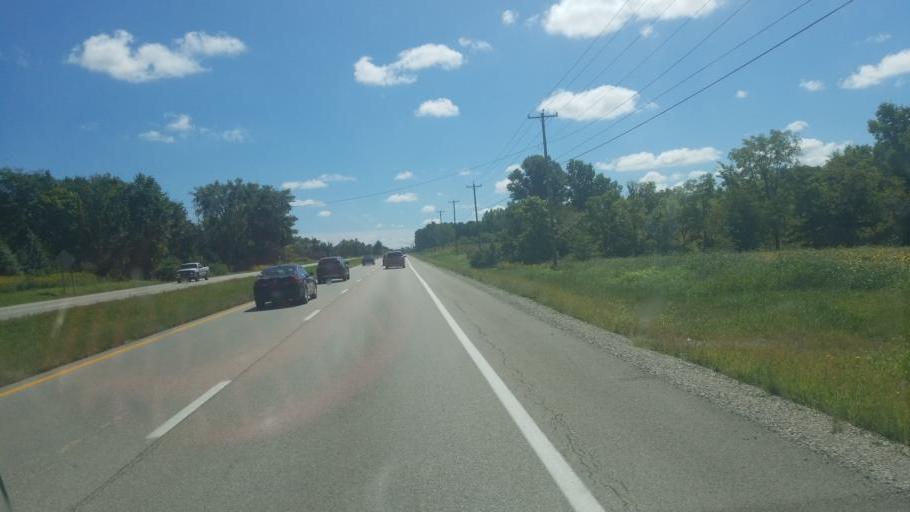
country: US
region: Ohio
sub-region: Delaware County
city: Lewis Center
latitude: 40.2390
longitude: -83.0485
